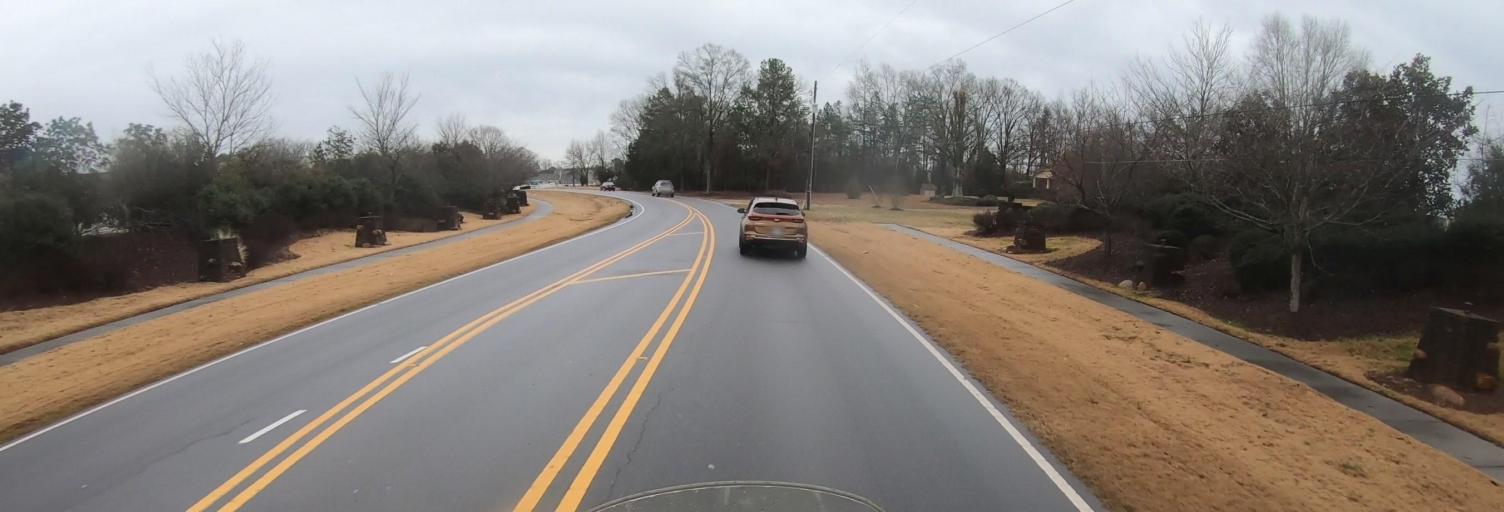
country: US
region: South Carolina
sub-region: York County
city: Tega Cay
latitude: 35.0706
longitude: -81.0002
